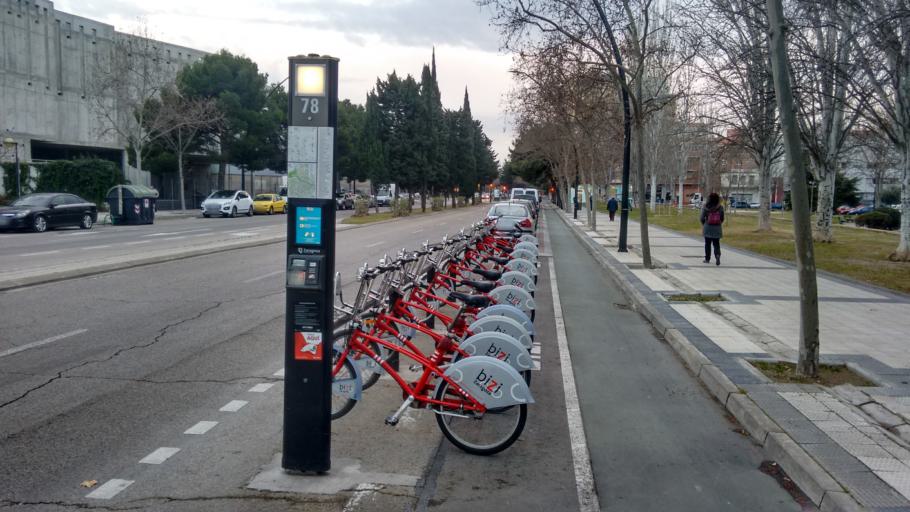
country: ES
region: Aragon
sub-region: Provincia de Zaragoza
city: Zaragoza
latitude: 41.6740
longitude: -0.8714
